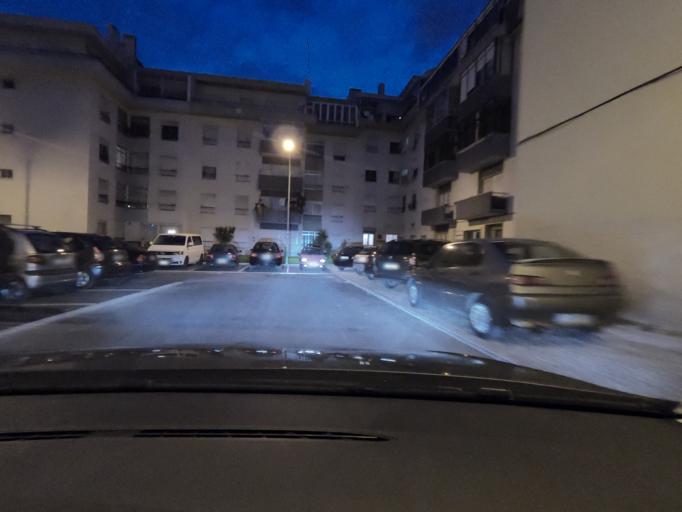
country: PT
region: Lisbon
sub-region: Oeiras
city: Carcavelos
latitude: 38.6944
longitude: -9.3253
